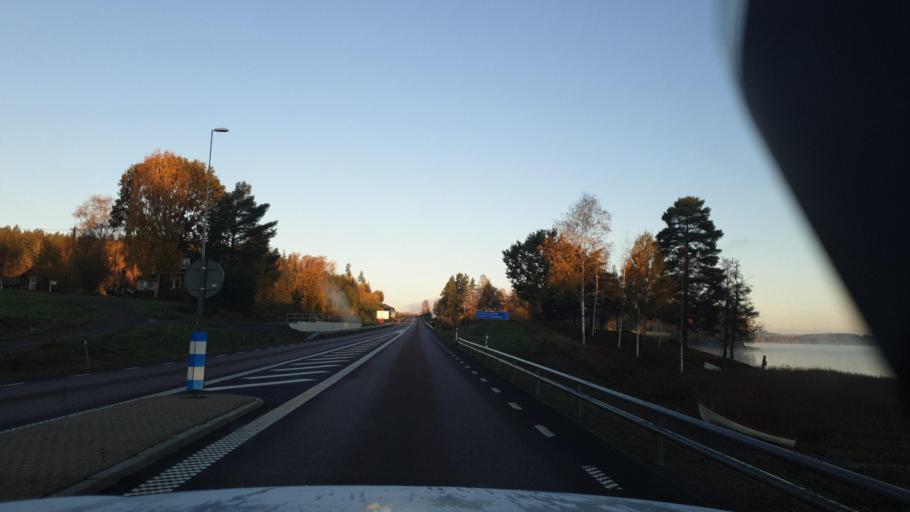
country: SE
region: Vaermland
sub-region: Eda Kommun
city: Amotfors
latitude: 59.7790
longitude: 12.3673
